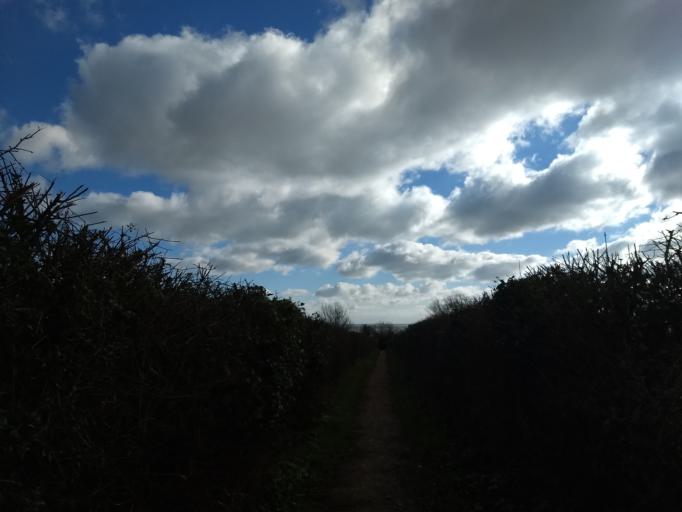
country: GB
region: England
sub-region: Isle of Wight
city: Bembridge
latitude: 50.6788
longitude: -1.0863
